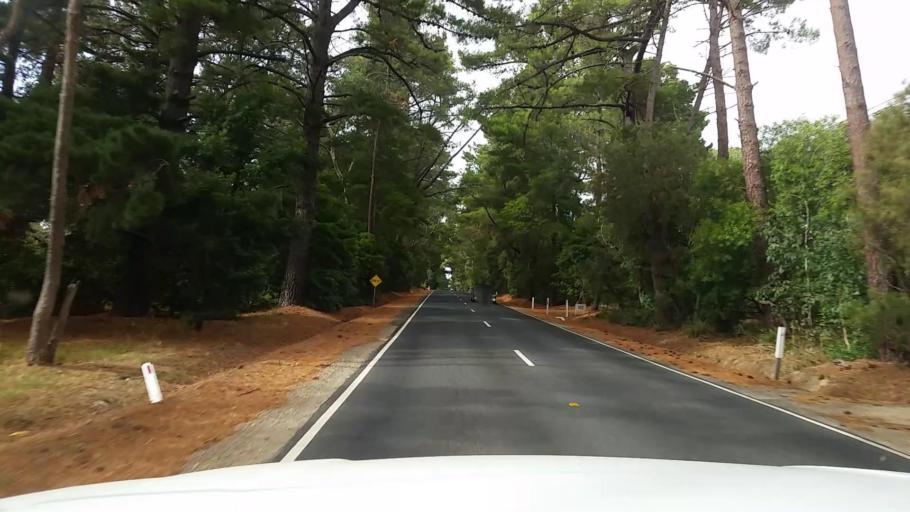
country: AU
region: Victoria
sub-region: Mornington Peninsula
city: Balnarring
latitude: -38.3648
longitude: 145.1179
